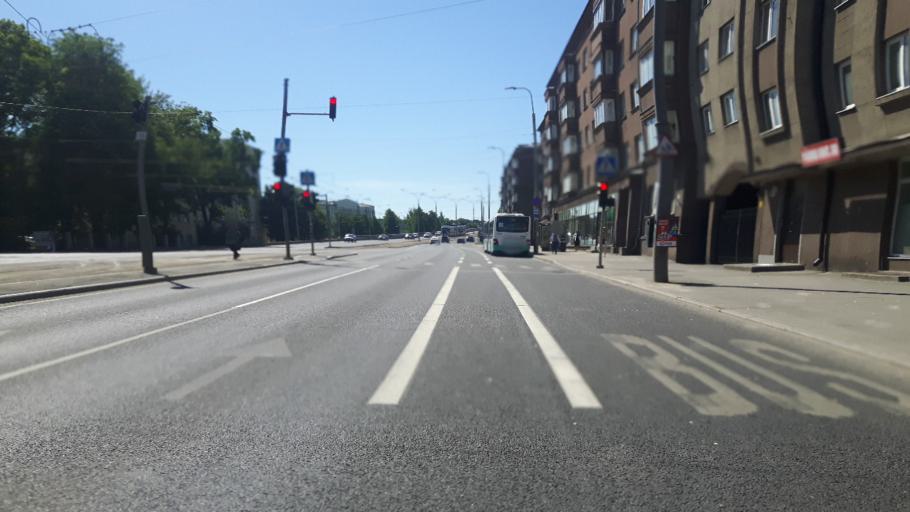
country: EE
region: Harju
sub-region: Tallinna linn
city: Tallinn
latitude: 59.4233
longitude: 24.7424
